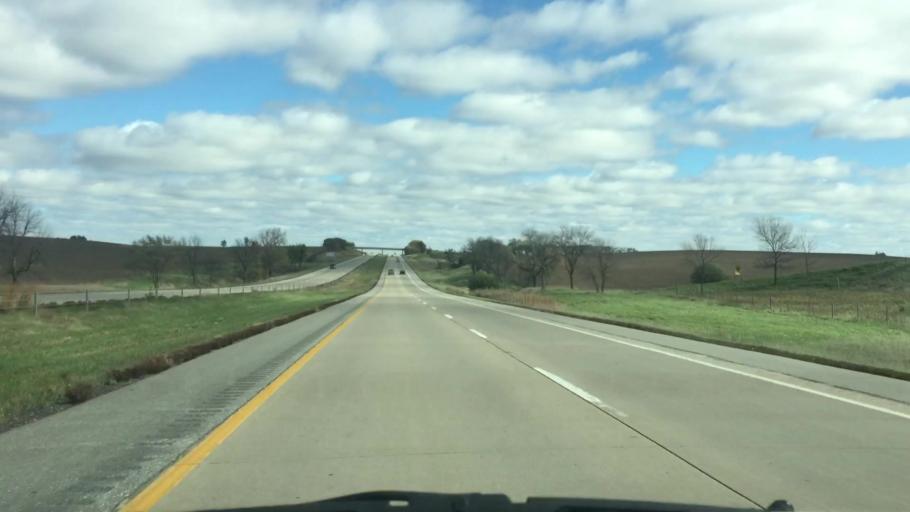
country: US
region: Iowa
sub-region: Poweshiek County
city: Brooklyn
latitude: 41.6955
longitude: -92.3301
